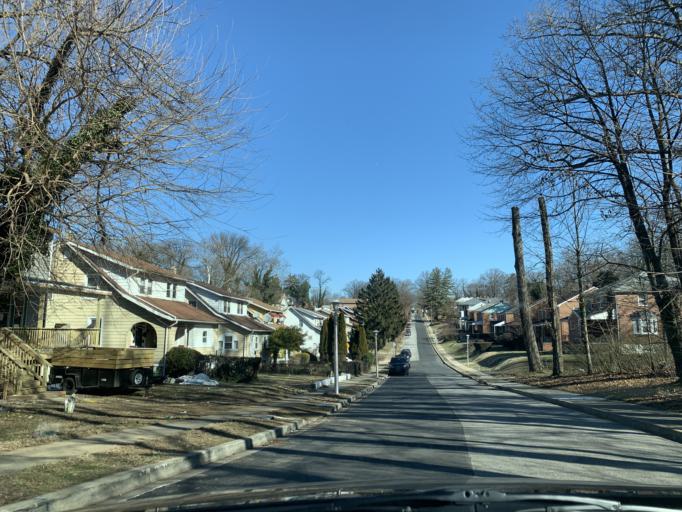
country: US
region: Maryland
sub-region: Baltimore County
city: Woodlawn
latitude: 39.3180
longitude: -76.6880
